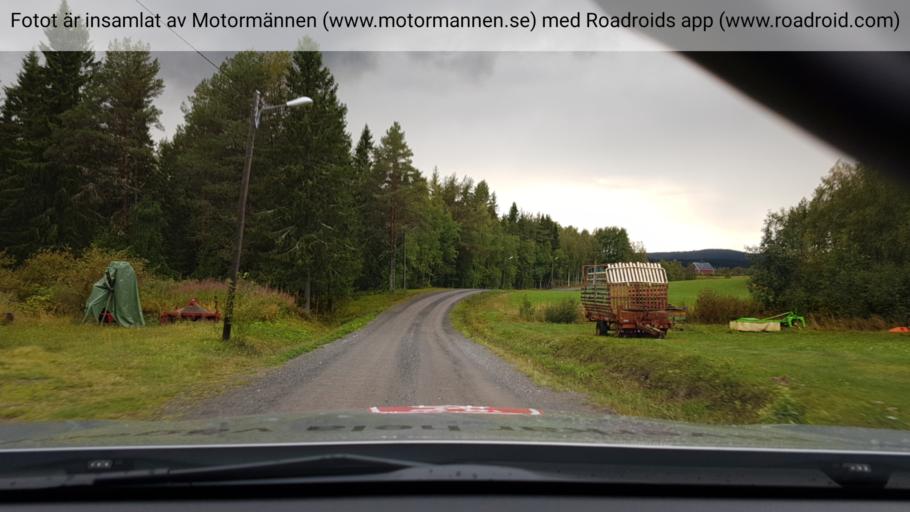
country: SE
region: Vaesterbotten
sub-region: Asele Kommun
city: Asele
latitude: 64.1833
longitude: 16.9226
